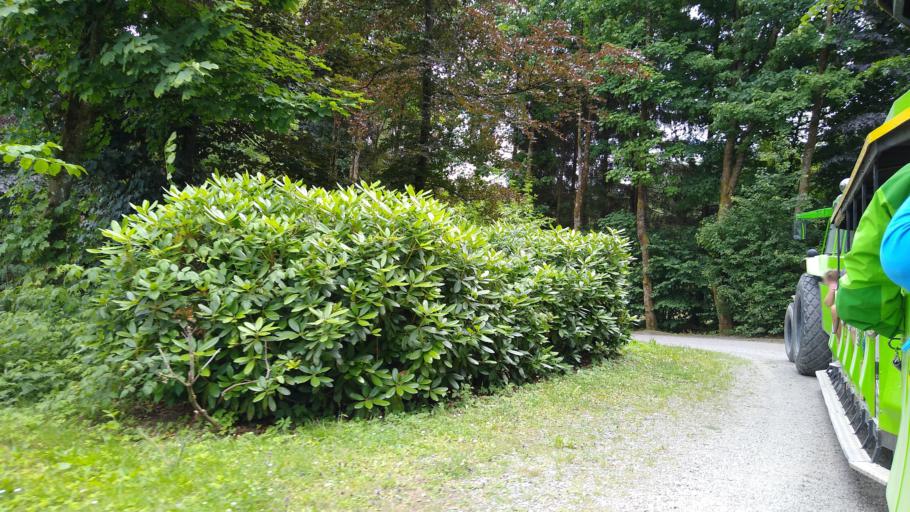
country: DE
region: North Rhine-Westphalia
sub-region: Regierungsbezirk Arnsberg
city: Kirchhundem
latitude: 51.0604
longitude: 8.1804
